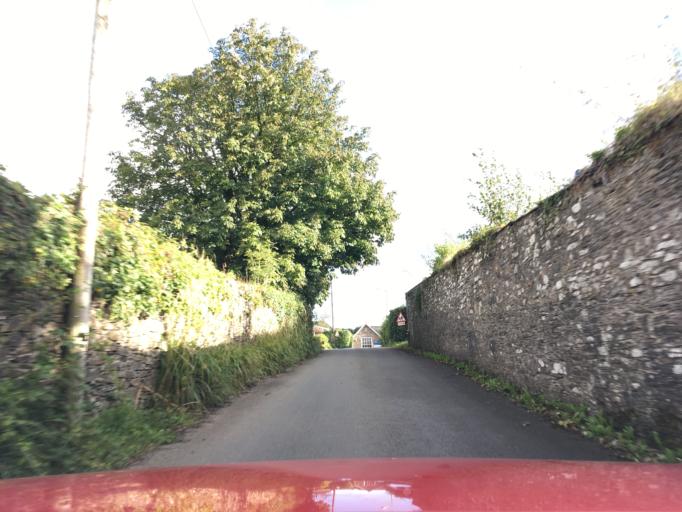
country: GB
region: England
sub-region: Devon
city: South Brent
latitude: 50.3976
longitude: -3.7915
